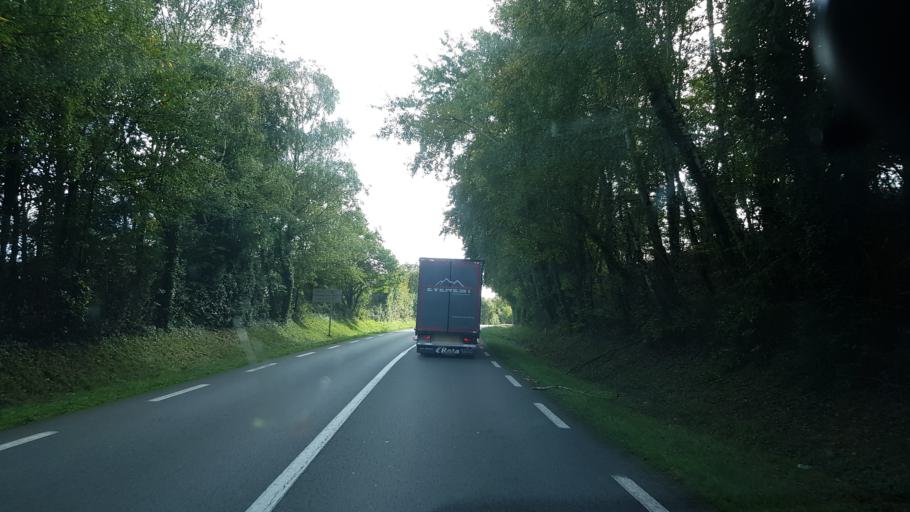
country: FR
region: Poitou-Charentes
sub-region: Departement de la Charente
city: Confolens
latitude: 46.0311
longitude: 0.6590
